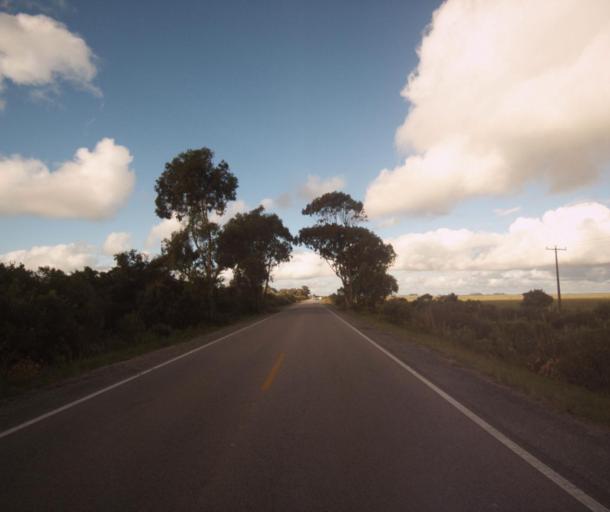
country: BR
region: Rio Grande do Sul
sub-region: Rio Grande
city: Rio Grande
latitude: -32.1887
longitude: -52.4315
